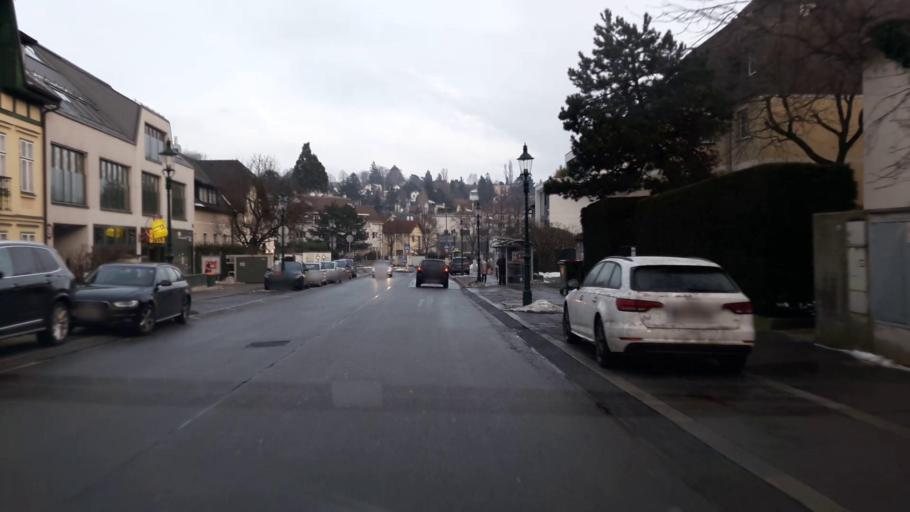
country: AT
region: Lower Austria
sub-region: Politischer Bezirk Wien-Umgebung
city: Klosterneuburg
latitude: 48.2506
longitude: 16.3061
